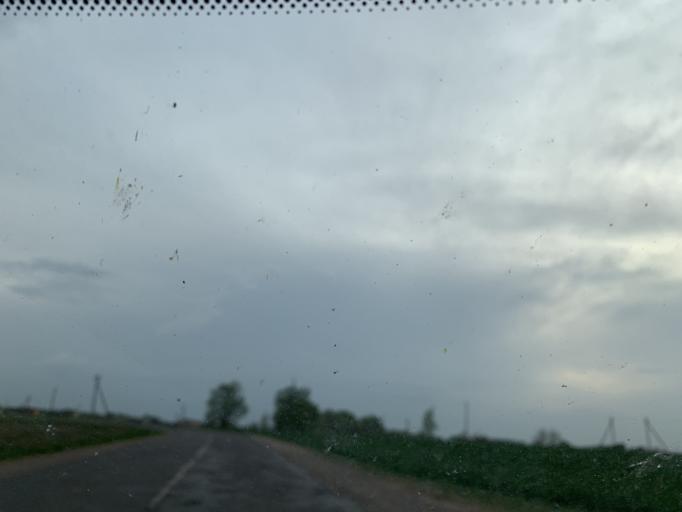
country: BY
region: Minsk
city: Kapyl'
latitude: 53.2688
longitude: 26.9589
